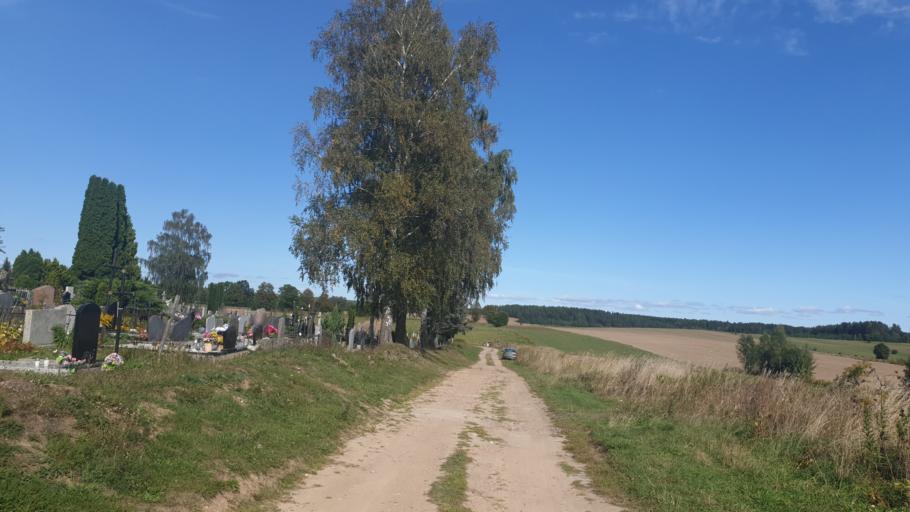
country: LT
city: Salcininkai
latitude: 54.4528
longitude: 25.5119
